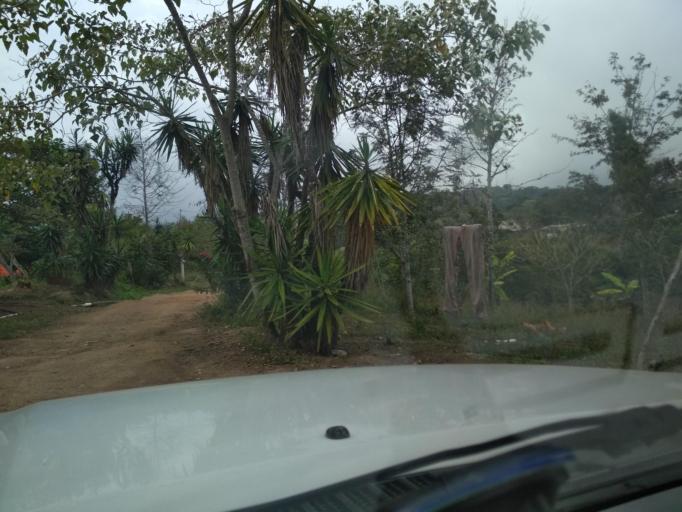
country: MX
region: Veracruz
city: El Castillo
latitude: 19.5372
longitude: -96.8336
